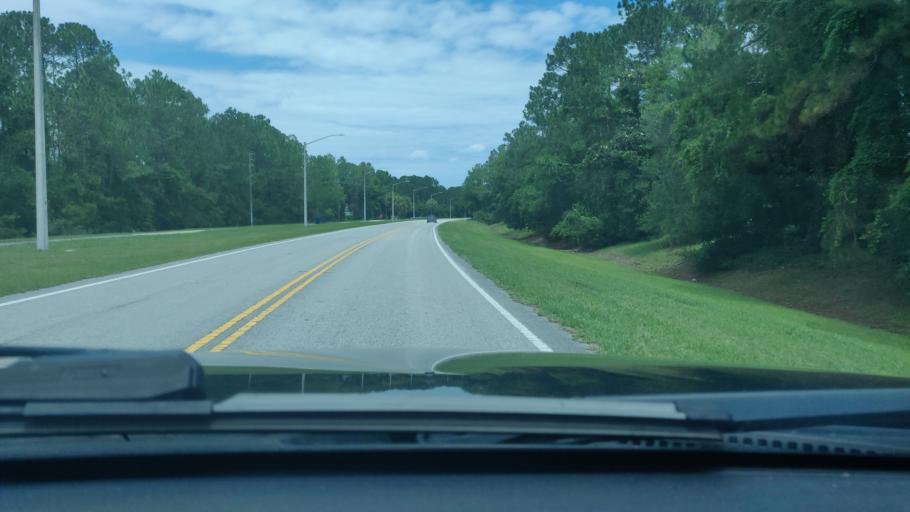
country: US
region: Florida
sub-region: Flagler County
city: Bunnell
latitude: 29.5337
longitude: -81.2535
